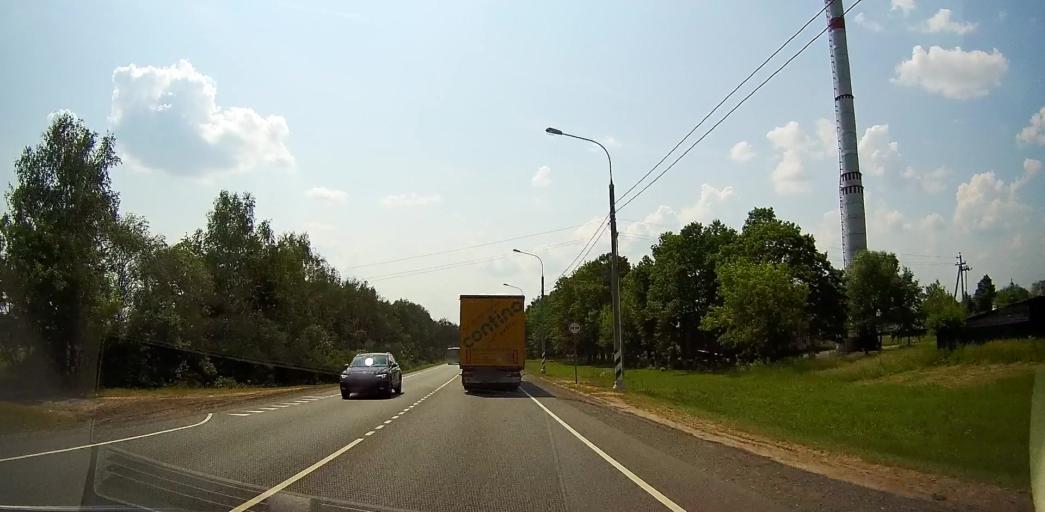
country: RU
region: Moskovskaya
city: Meshcherino
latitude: 55.1963
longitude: 38.3681
